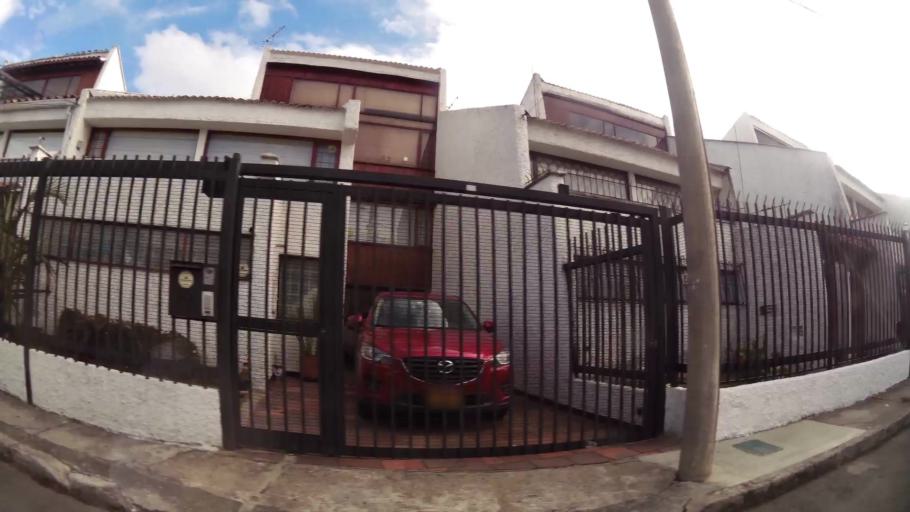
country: CO
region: Bogota D.C.
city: Barrio San Luis
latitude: 4.6917
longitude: -74.0710
